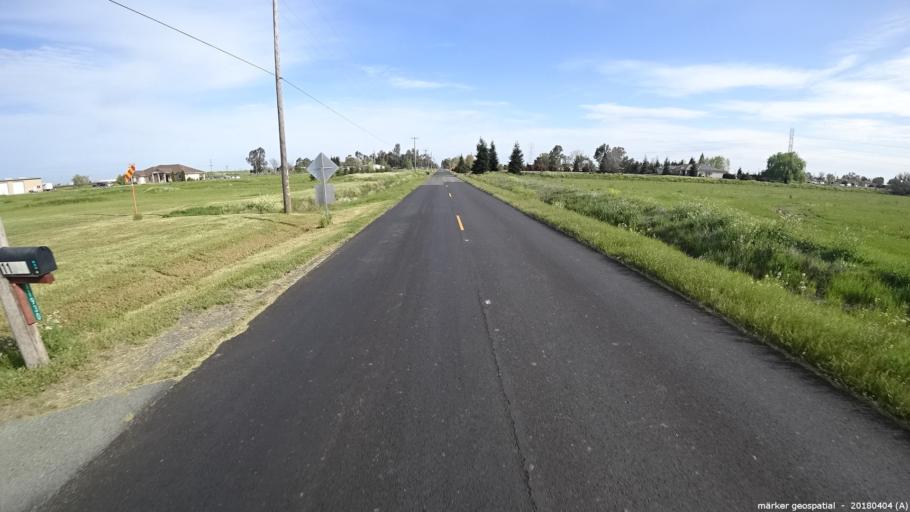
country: US
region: California
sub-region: Sacramento County
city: Herald
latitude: 38.3227
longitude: -121.2421
